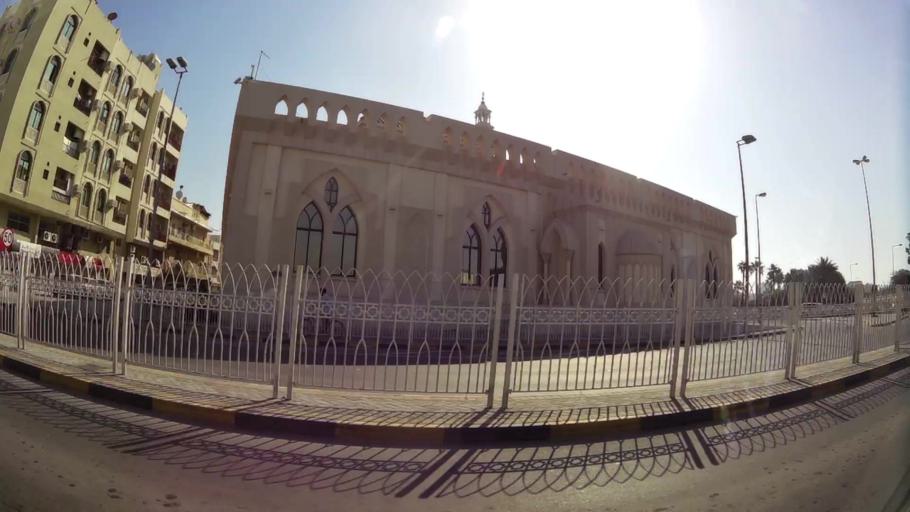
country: BH
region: Manama
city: Manama
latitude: 26.2241
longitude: 50.5878
